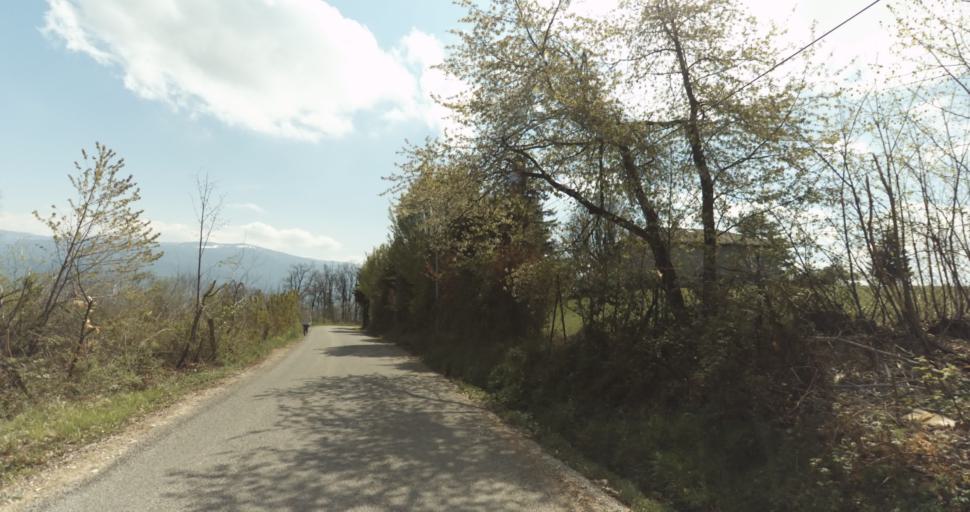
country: FR
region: Rhone-Alpes
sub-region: Departement de l'Isere
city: Saint-Marcellin
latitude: 45.1692
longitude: 5.3092
